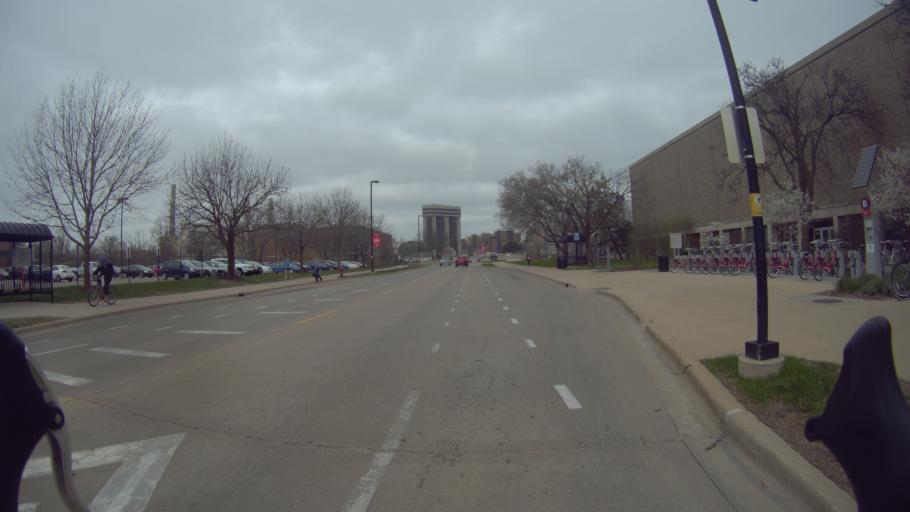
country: US
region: Wisconsin
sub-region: Dane County
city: Madison
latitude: 43.0765
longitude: -89.4201
